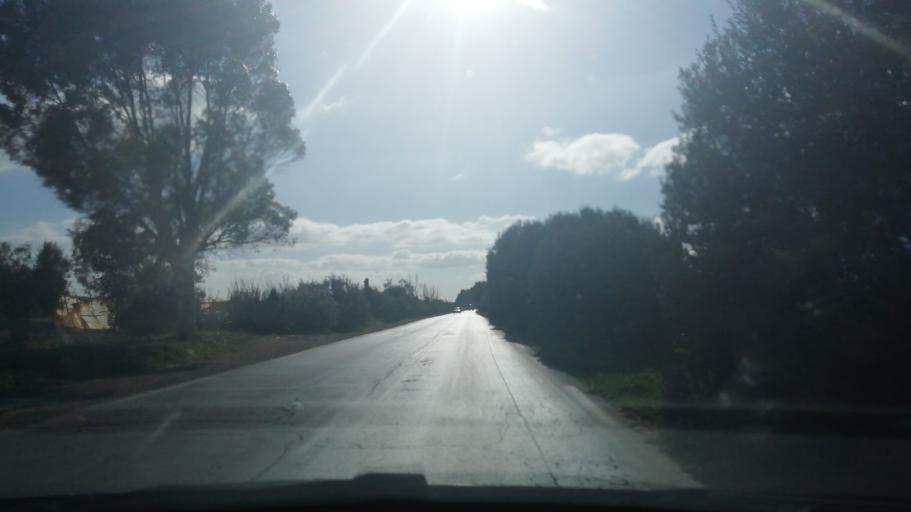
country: DZ
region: Mostaganem
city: Mostaganem
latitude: 35.9577
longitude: 0.2478
